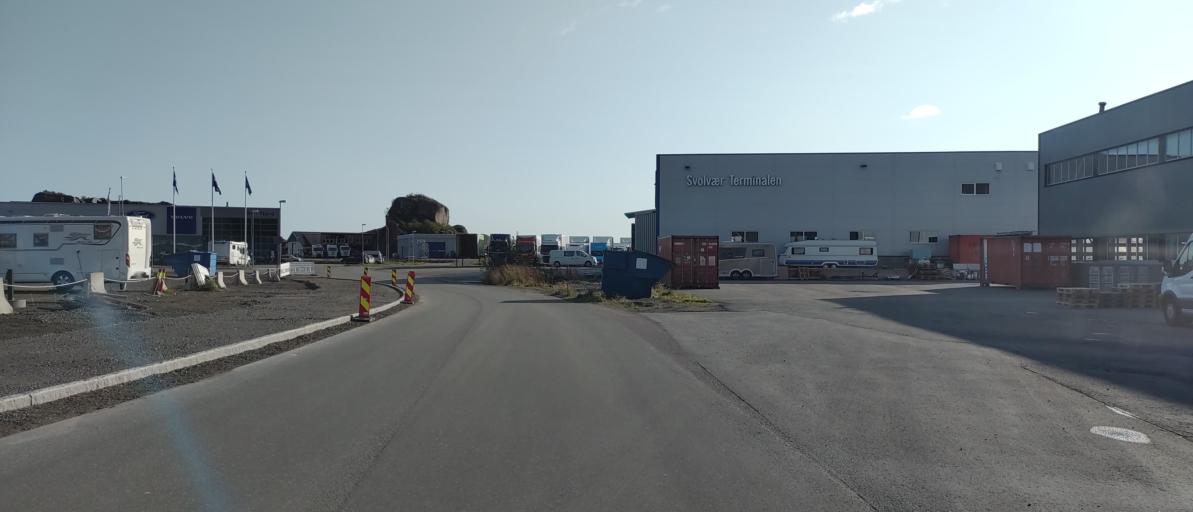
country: NO
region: Nordland
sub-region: Vagan
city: Svolvaer
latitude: 68.2278
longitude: 14.5559
